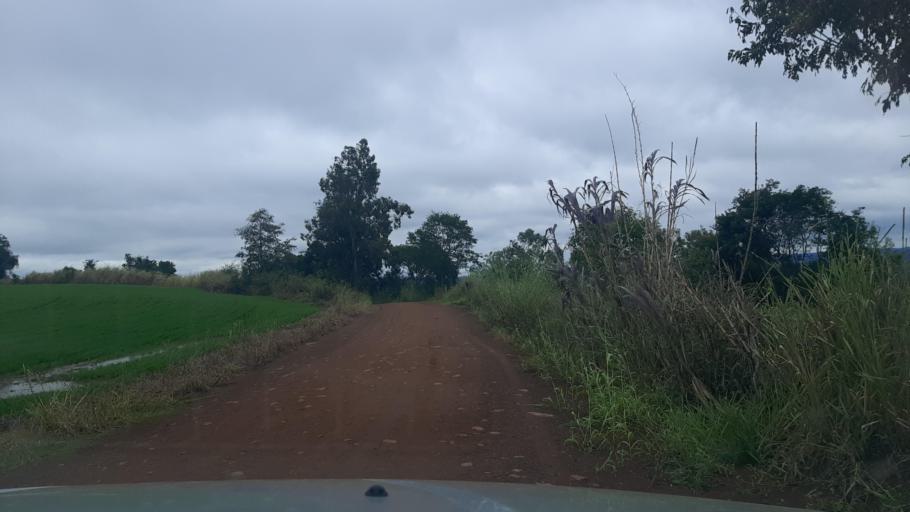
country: BR
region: Parana
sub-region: Ampere
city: Ampere
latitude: -26.0538
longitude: -53.5535
